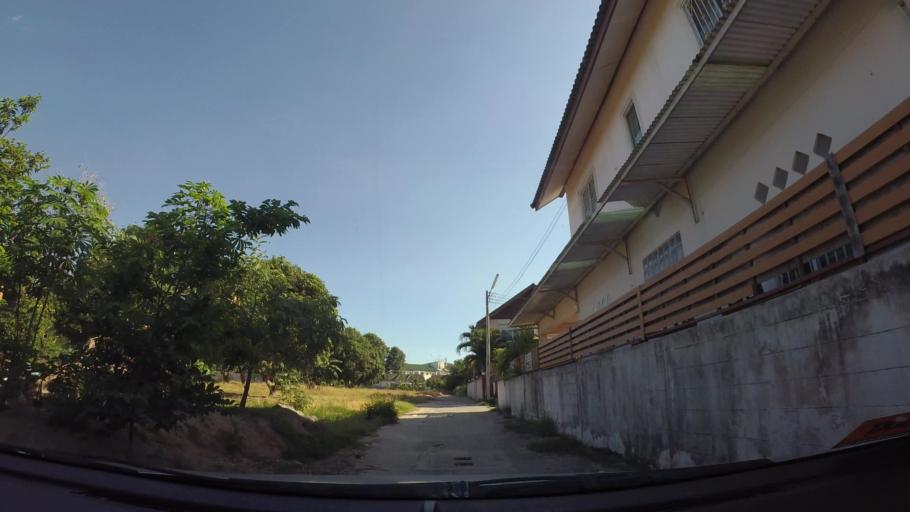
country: TH
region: Chon Buri
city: Si Racha
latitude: 13.1508
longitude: 100.9388
